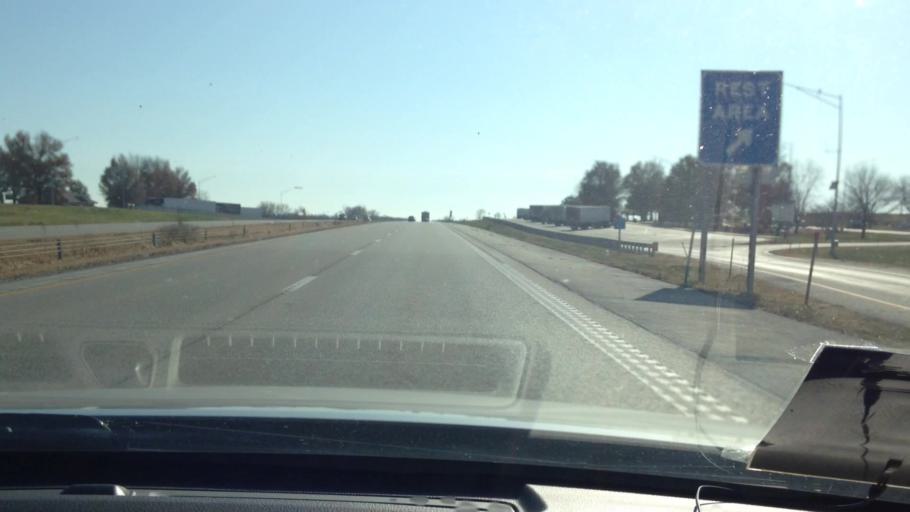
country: US
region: Missouri
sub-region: Platte County
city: Platte City
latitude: 39.4784
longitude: -94.7872
